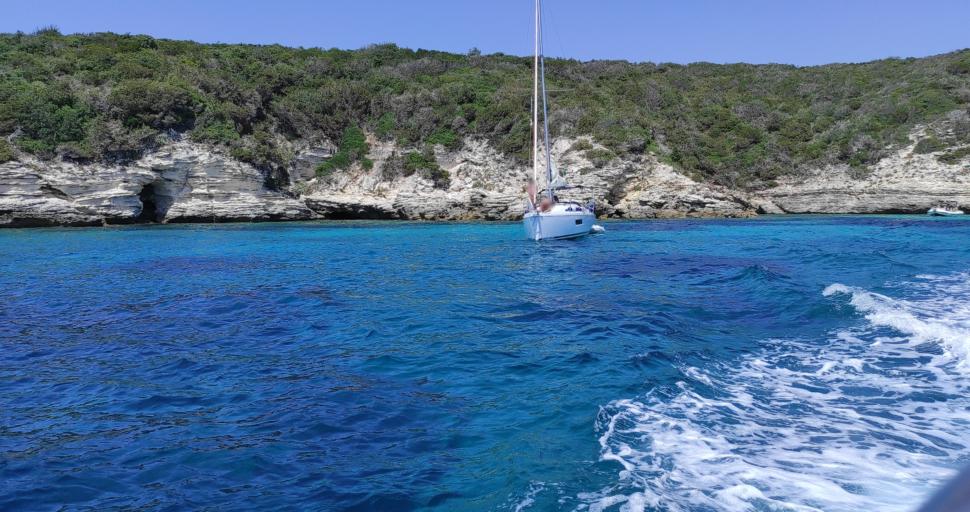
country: FR
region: Corsica
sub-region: Departement de la Corse-du-Sud
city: Bonifacio
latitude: 41.3937
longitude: 9.1336
